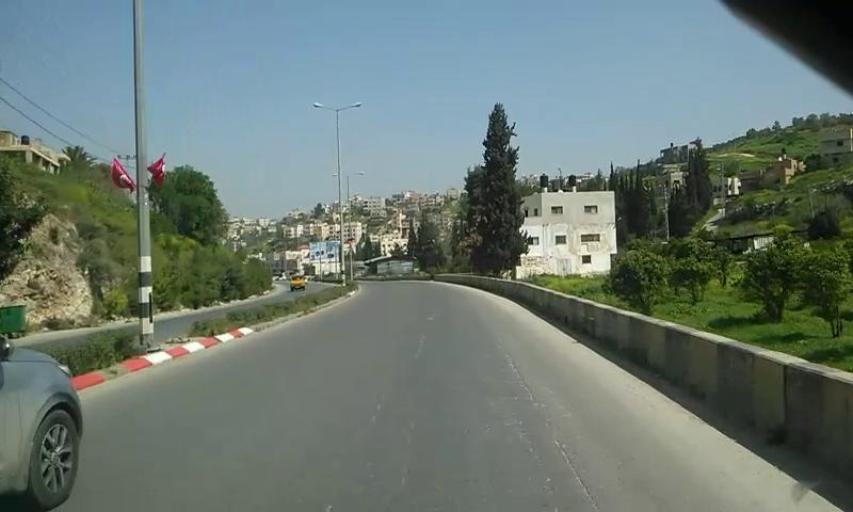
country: PS
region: West Bank
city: Janin
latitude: 32.4440
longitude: 35.2931
